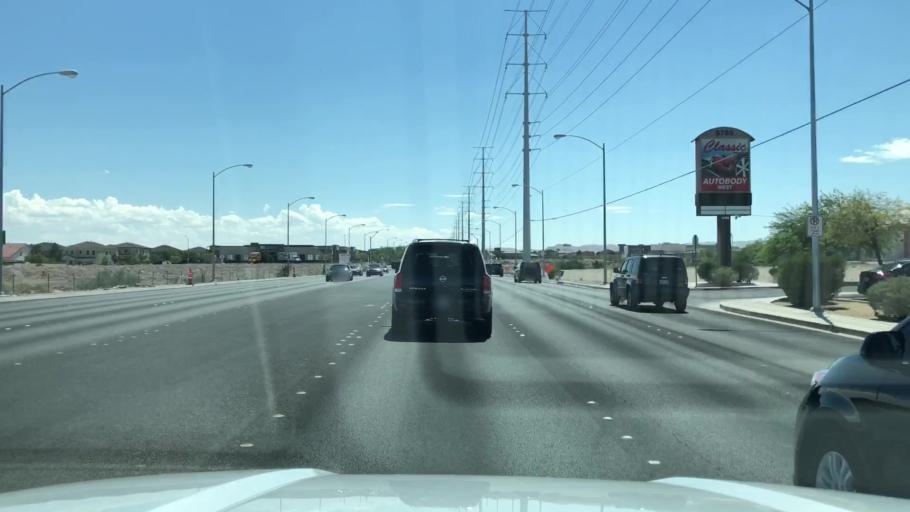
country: US
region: Nevada
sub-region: Clark County
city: Spring Valley
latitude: 36.0838
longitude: -115.2793
